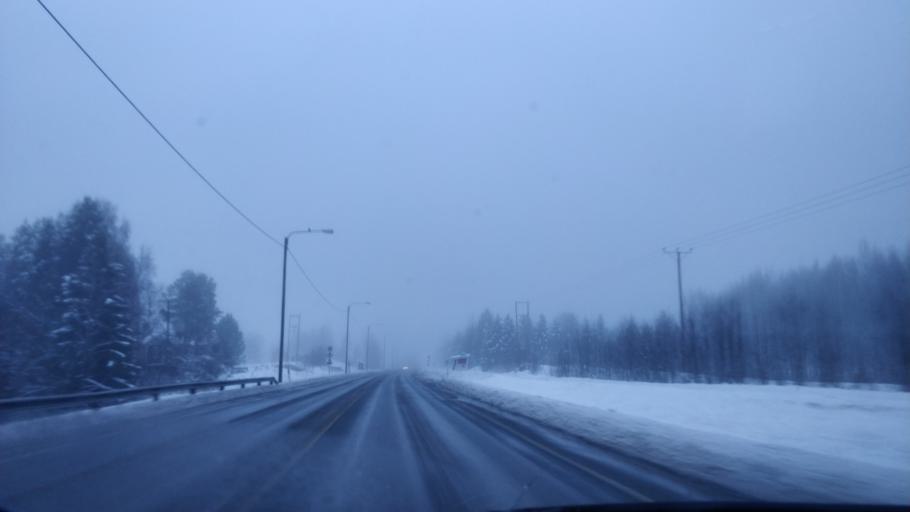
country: FI
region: Lapland
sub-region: Kemi-Tornio
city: Tervola
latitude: 66.1416
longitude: 24.9489
